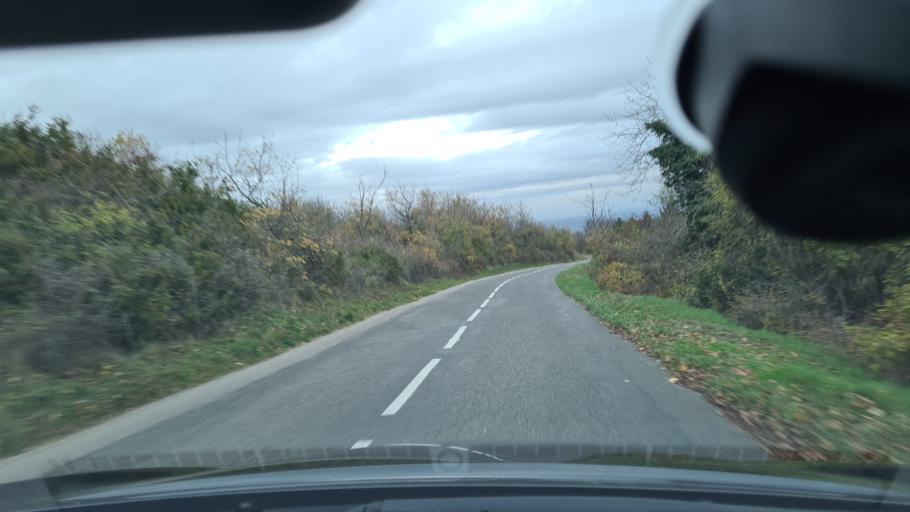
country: FR
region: Rhone-Alpes
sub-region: Departement du Rhone
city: Limonest
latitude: 45.8523
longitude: 4.7831
